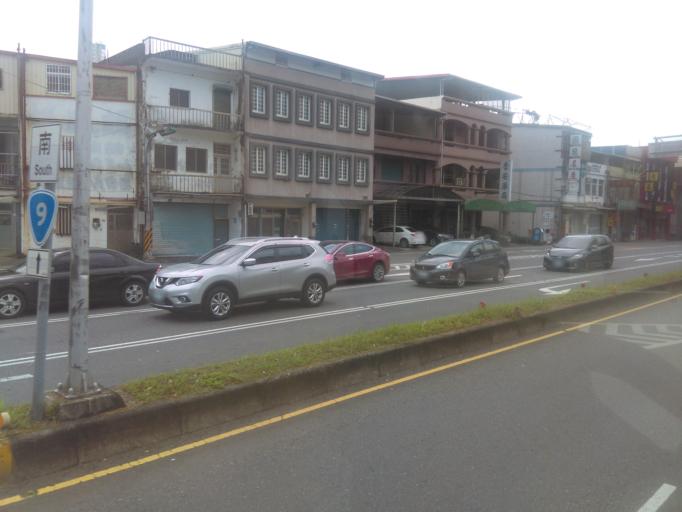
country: TW
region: Taiwan
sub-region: Yilan
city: Yilan
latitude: 24.8383
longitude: 121.7907
